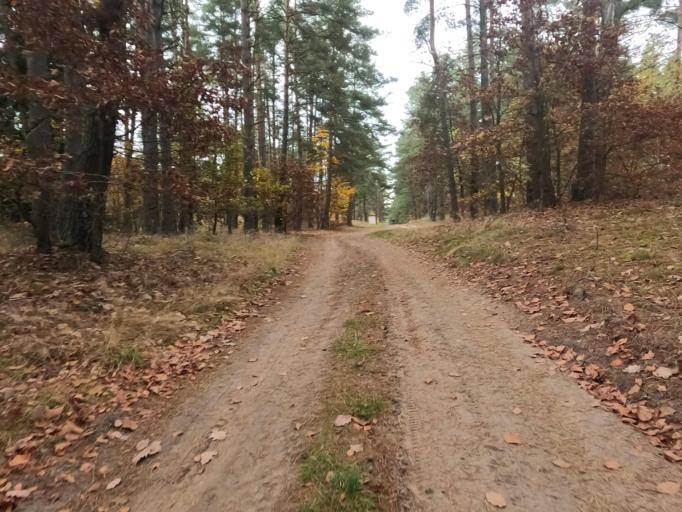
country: PL
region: Pomeranian Voivodeship
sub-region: Powiat starogardzki
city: Skarszewy
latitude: 54.0546
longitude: 18.4427
